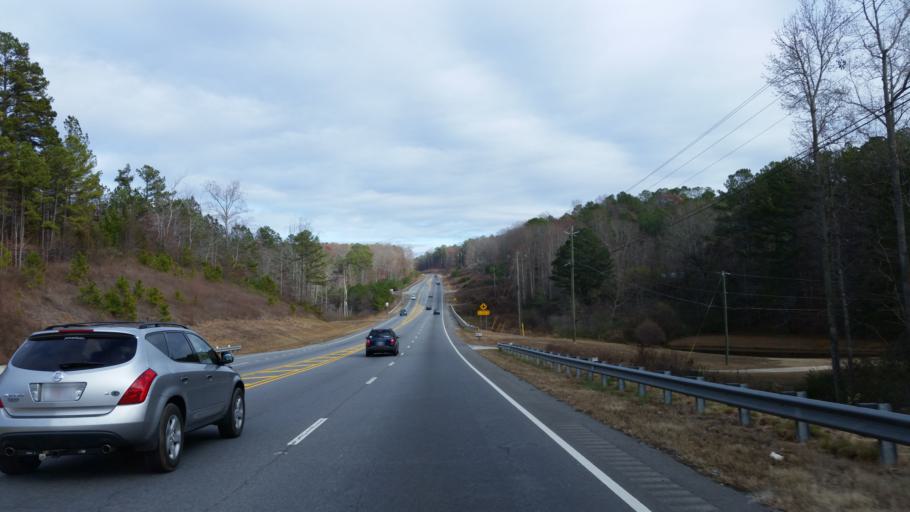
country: US
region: Georgia
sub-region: Bartow County
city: Cartersville
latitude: 34.2200
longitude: -84.7250
